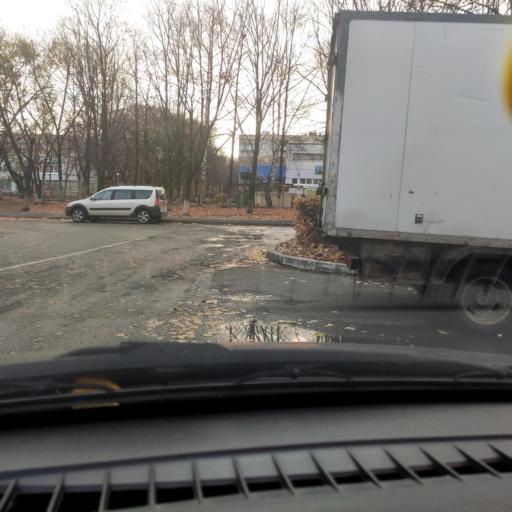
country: RU
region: Samara
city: Tol'yatti
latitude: 53.5233
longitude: 49.2901
